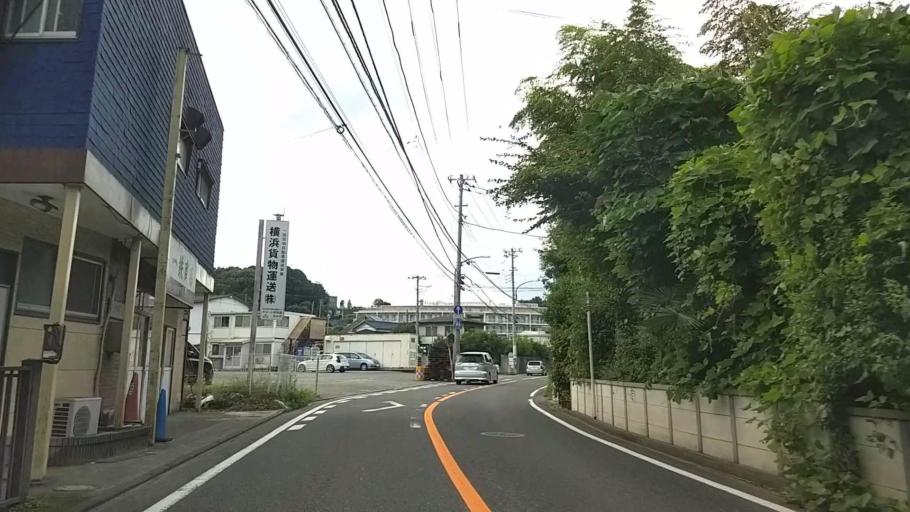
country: JP
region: Kanagawa
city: Yokohama
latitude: 35.4927
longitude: 139.5695
